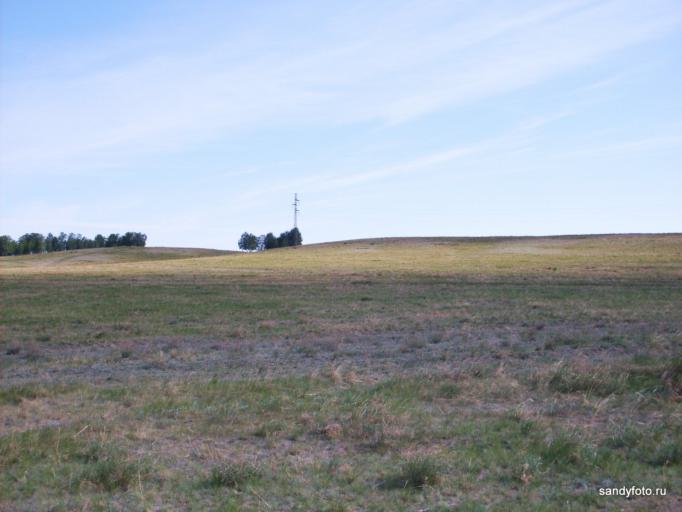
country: RU
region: Chelyabinsk
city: Troitsk
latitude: 54.1290
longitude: 61.4608
